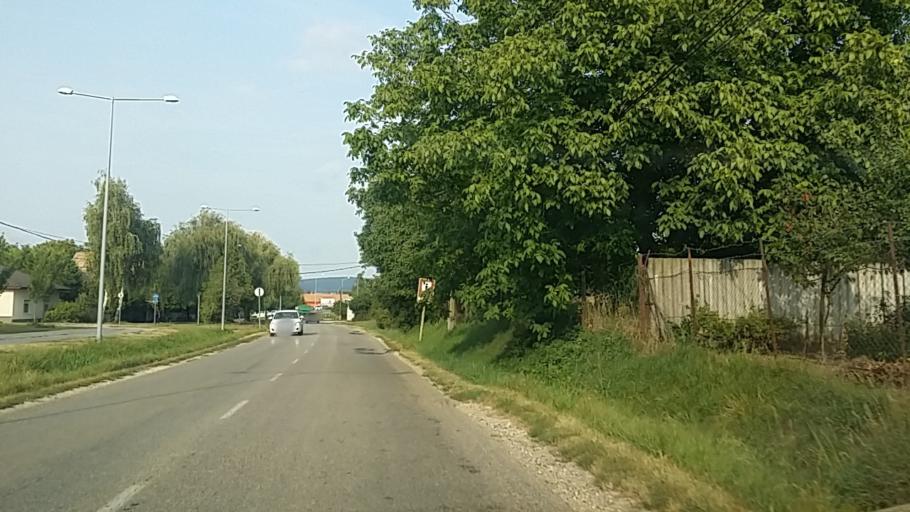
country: HU
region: Komarom-Esztergom
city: Tata
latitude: 47.6379
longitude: 18.3032
